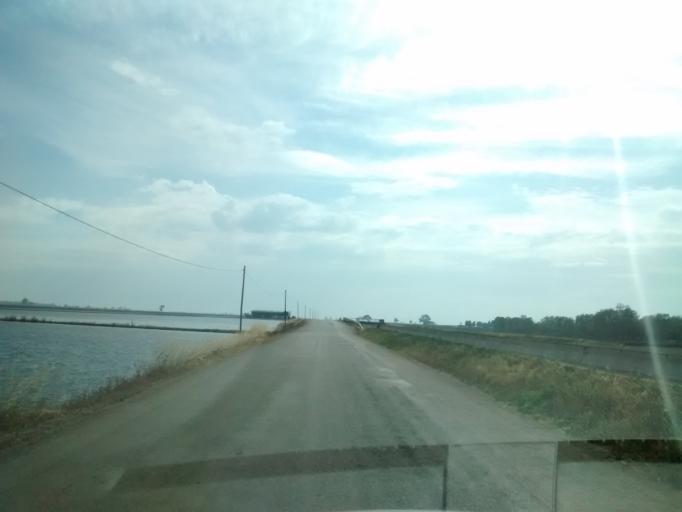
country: ES
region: Catalonia
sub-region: Provincia de Tarragona
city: Deltebre
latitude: 40.6973
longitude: 0.8077
